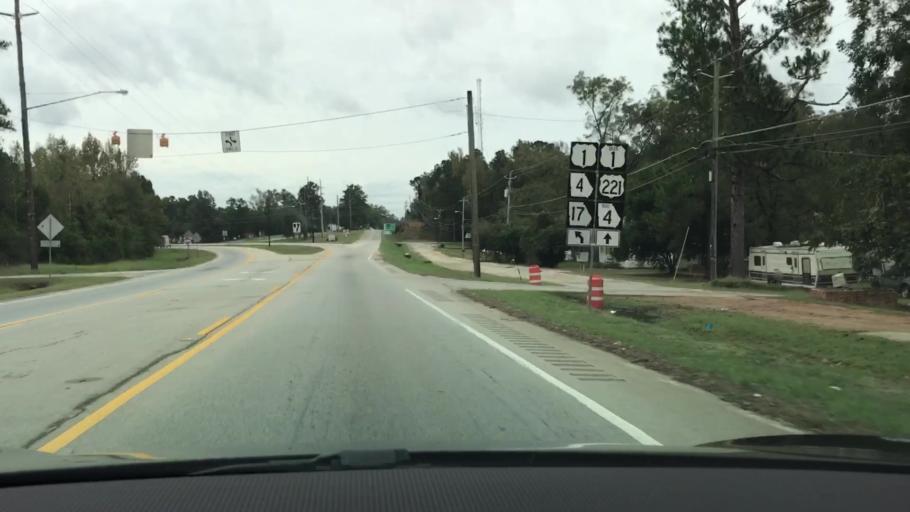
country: US
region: Georgia
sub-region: Jefferson County
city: Louisville
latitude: 33.0184
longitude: -82.4044
